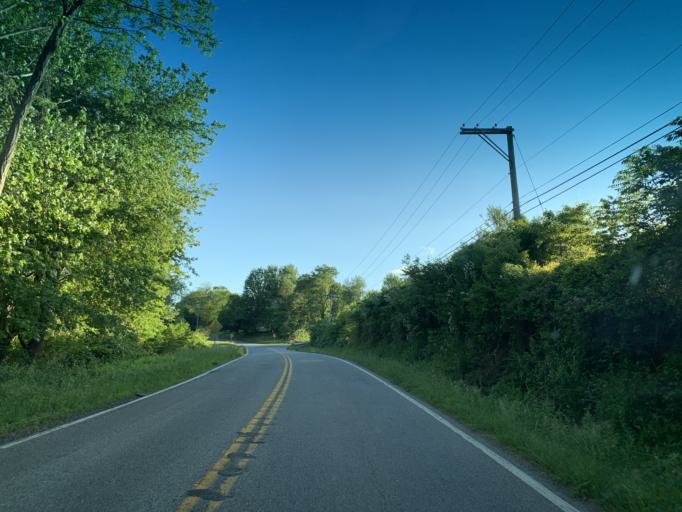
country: US
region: Maryland
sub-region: Cecil County
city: Elkton
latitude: 39.6664
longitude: -75.8404
